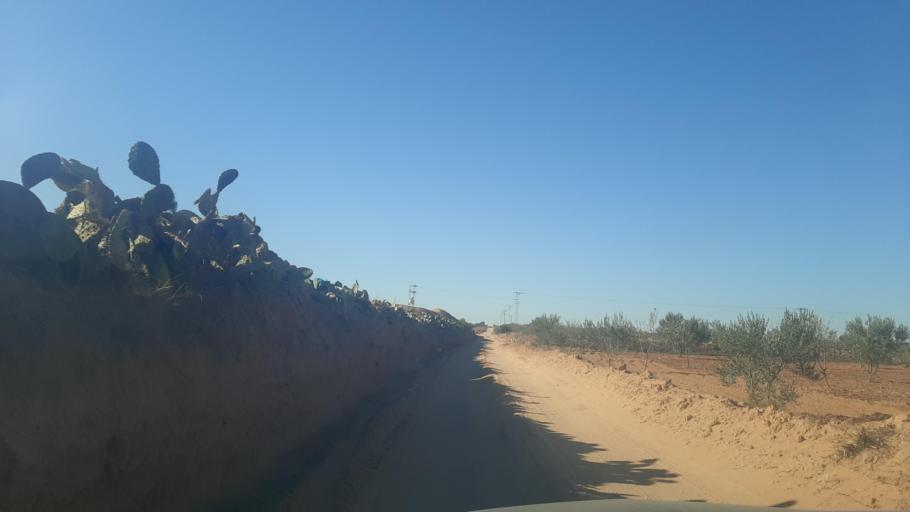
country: TN
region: Safaqis
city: Sfax
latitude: 34.8932
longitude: 10.5944
